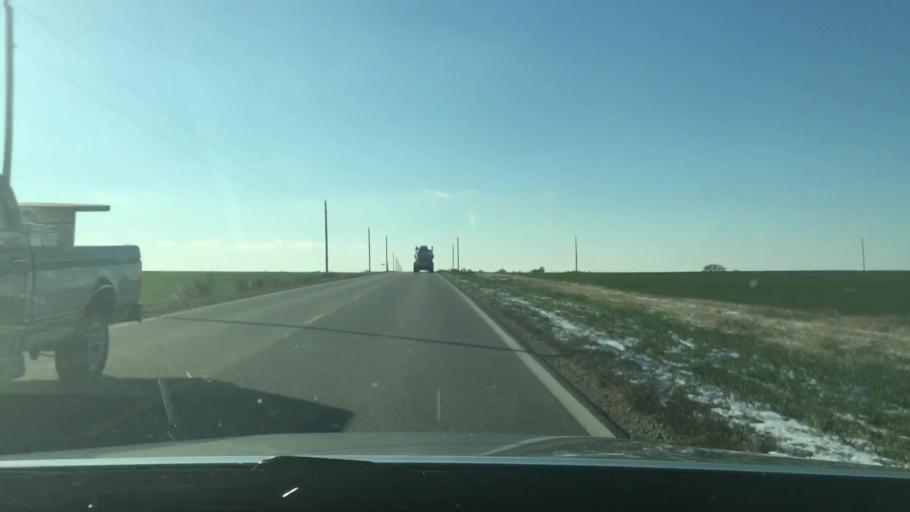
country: US
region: Kansas
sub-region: Reno County
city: Nickerson
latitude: 38.1450
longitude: -98.1580
